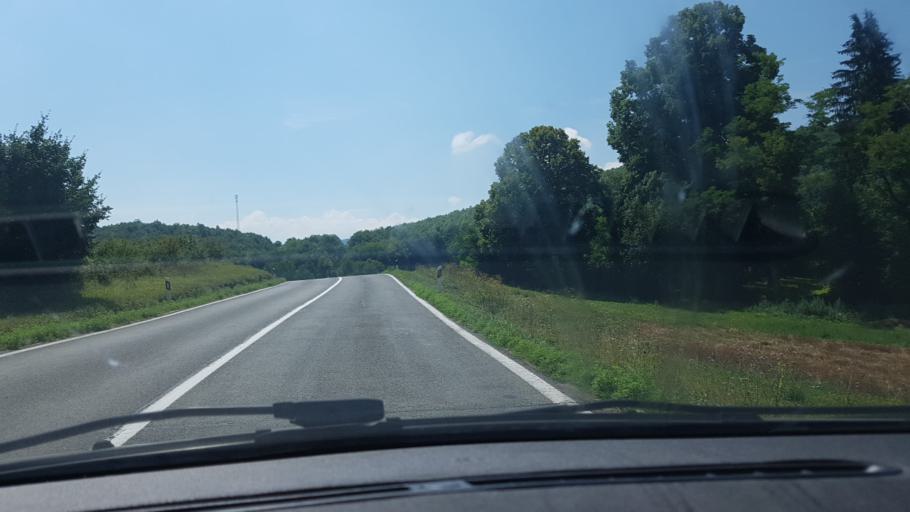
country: HR
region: Licko-Senjska
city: Otocac
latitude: 44.8830
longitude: 15.1980
